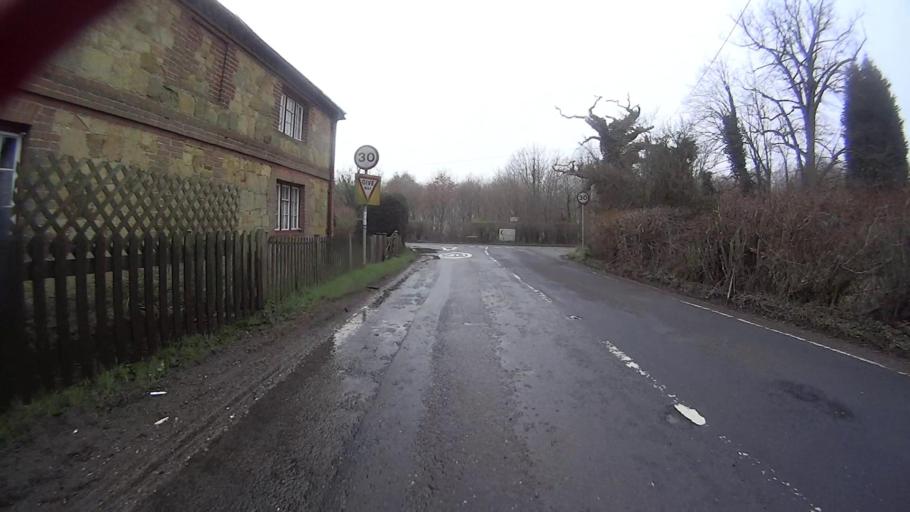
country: GB
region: England
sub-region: Surrey
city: Ockley
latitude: 51.1531
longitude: -0.3574
